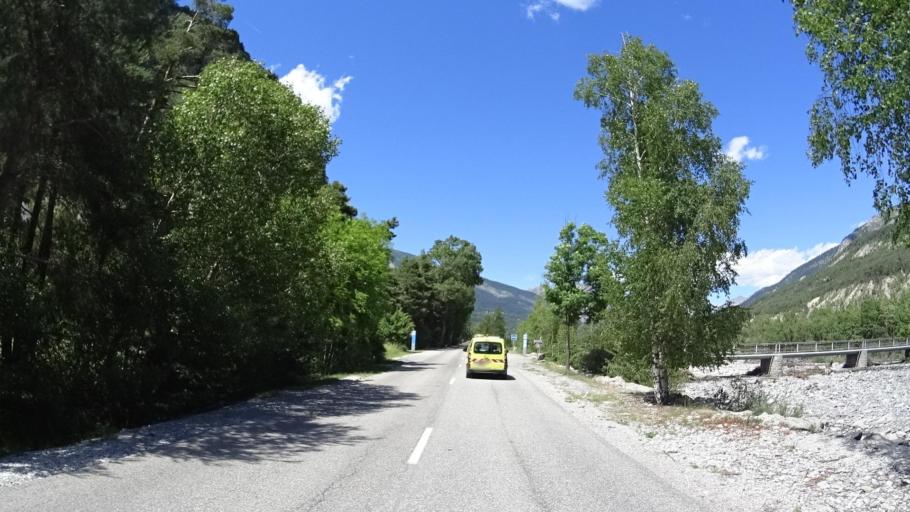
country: FR
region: Provence-Alpes-Cote d'Azur
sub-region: Departement des Alpes-de-Haute-Provence
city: Annot
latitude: 44.1124
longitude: 6.5794
